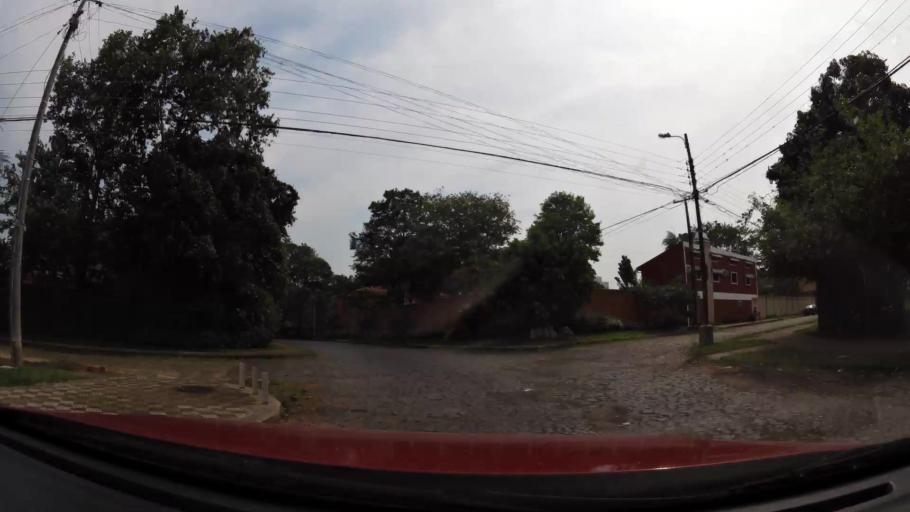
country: PY
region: Central
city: Fernando de la Mora
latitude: -25.2711
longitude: -57.5599
